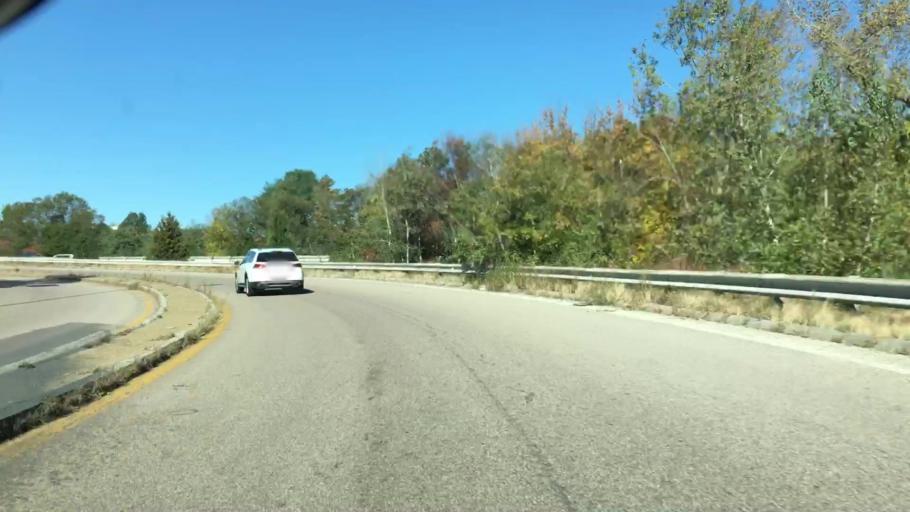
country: US
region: Massachusetts
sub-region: Middlesex County
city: Framingham Center
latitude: 42.2983
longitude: -71.4745
